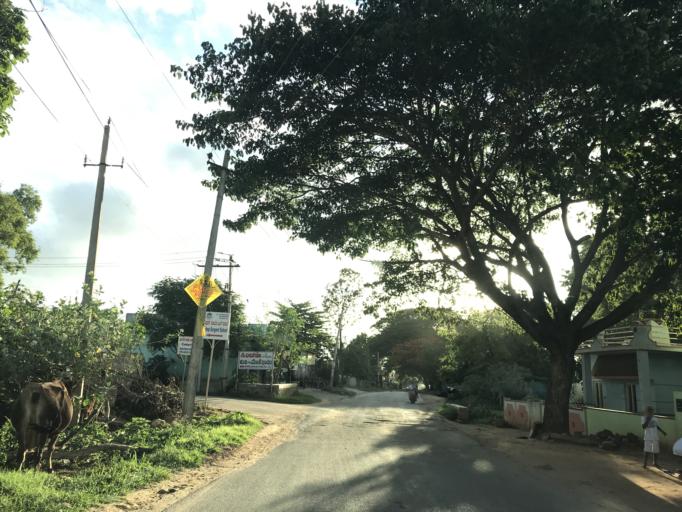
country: IN
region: Karnataka
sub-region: Bangalore Urban
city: Yelahanka
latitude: 13.1325
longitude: 77.6869
